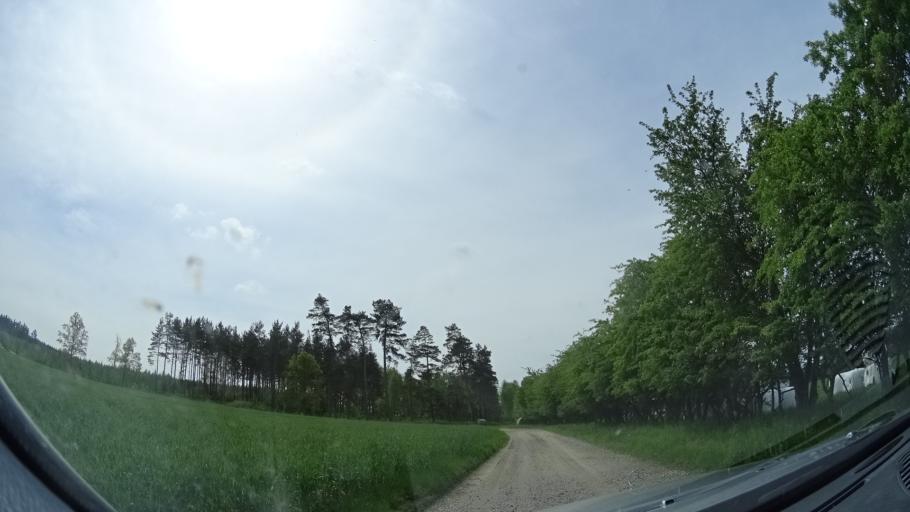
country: SE
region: Skane
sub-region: Sjobo Kommun
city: Sjoebo
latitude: 55.6734
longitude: 13.6294
